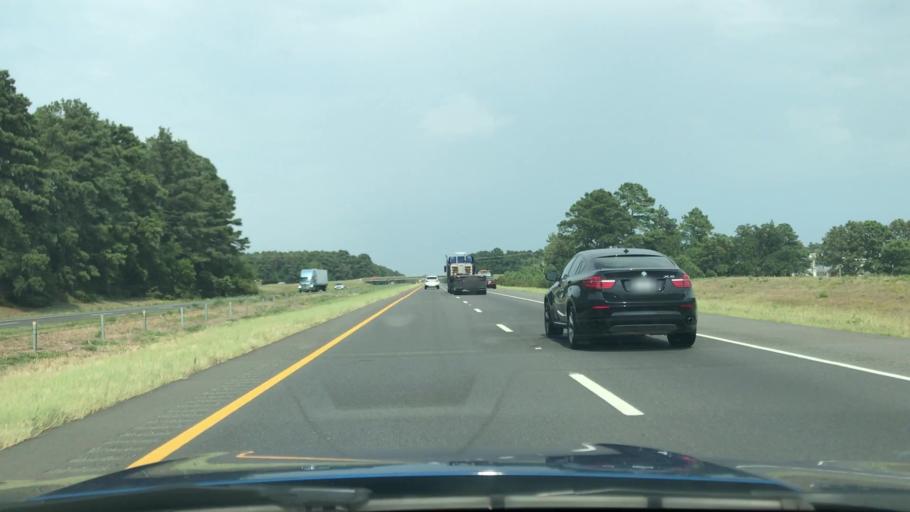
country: US
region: Texas
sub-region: Harrison County
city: Hallsville
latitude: 32.4657
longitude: -94.6278
